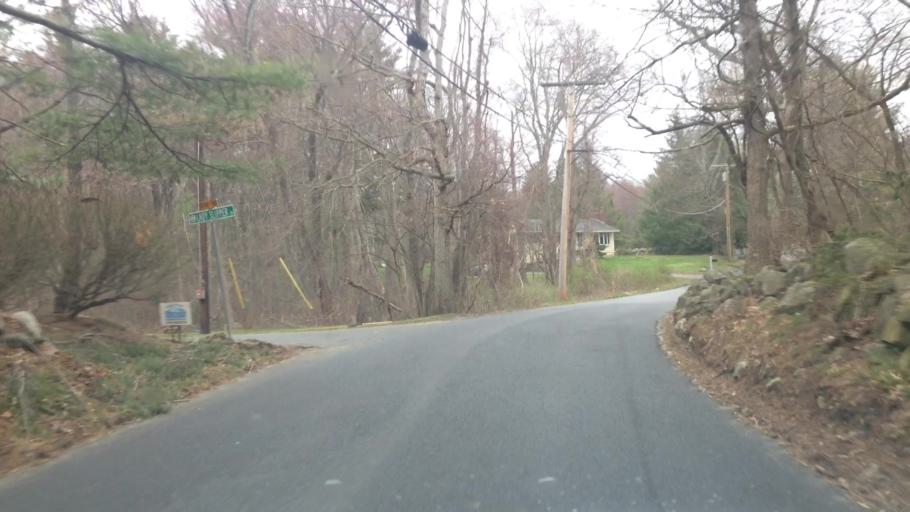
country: US
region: Massachusetts
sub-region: Middlesex County
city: Acton
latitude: 42.4921
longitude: -71.4091
